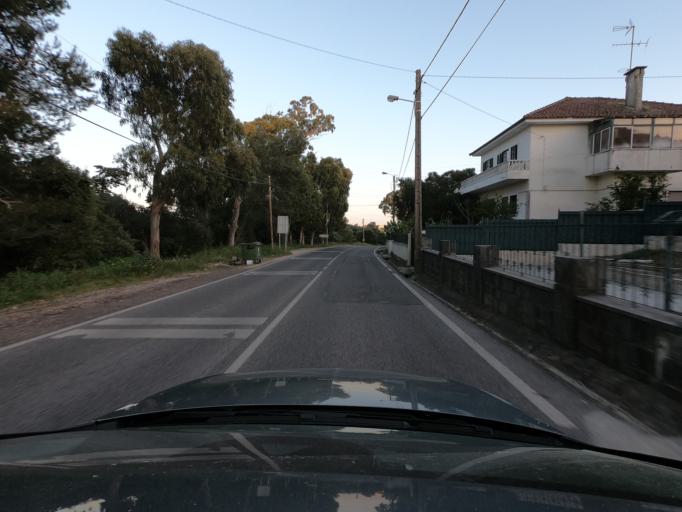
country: PT
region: Lisbon
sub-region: Sintra
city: Rio de Mouro
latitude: 38.7573
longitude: -9.3452
